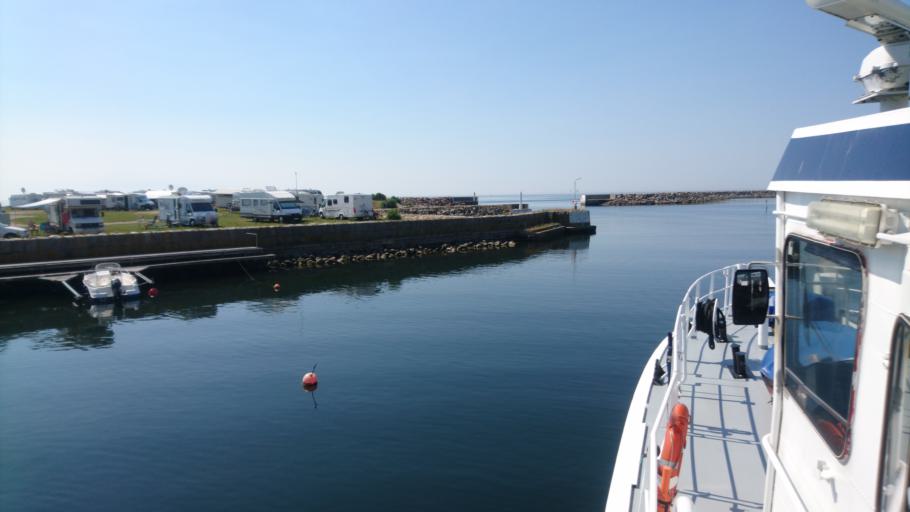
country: SE
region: Blekinge
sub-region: Solvesborgs Kommun
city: Soelvesborg
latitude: 56.0041
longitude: 14.7363
